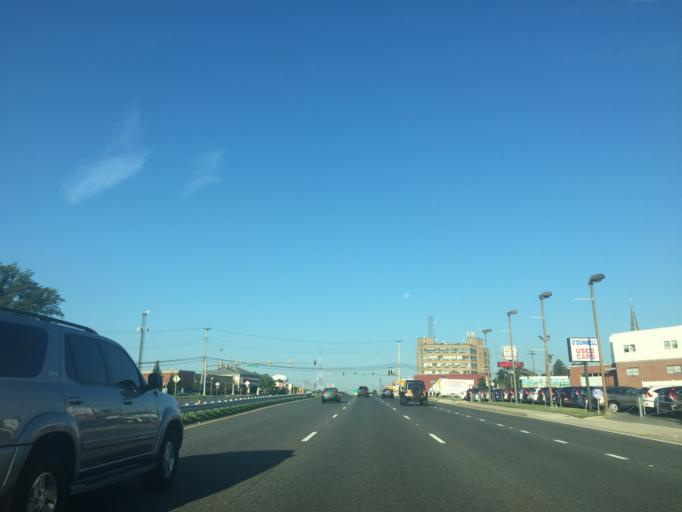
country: US
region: Maryland
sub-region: Baltimore County
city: Catonsville
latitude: 39.2902
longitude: -76.7232
